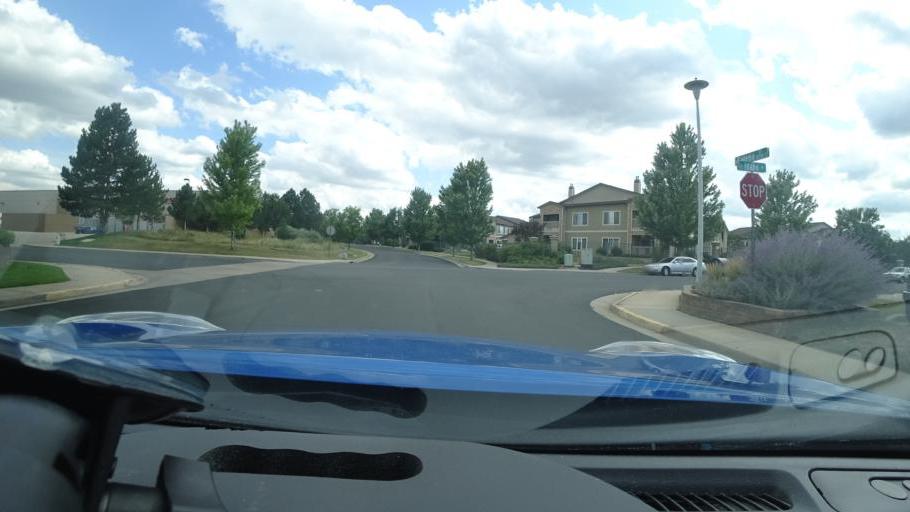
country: US
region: Colorado
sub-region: Adams County
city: Aurora
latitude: 39.6919
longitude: -104.8698
